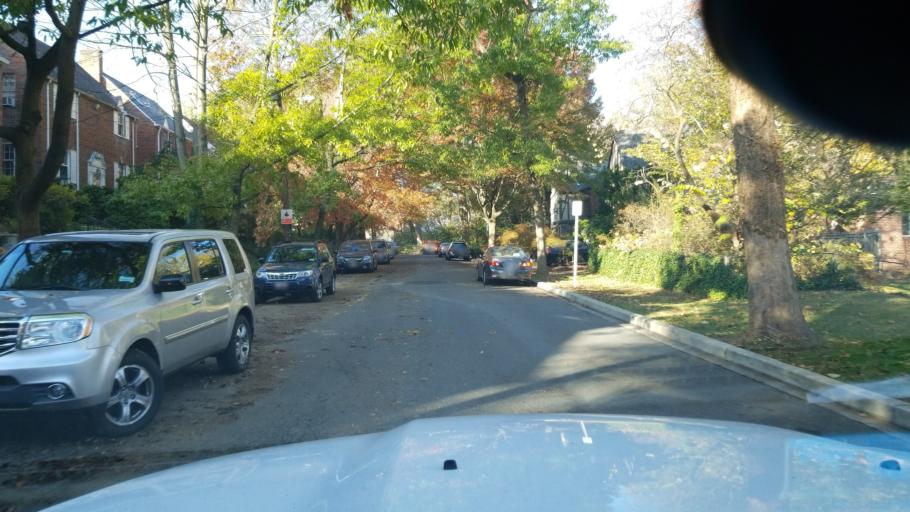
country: US
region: Maryland
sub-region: Montgomery County
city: Chevy Chase Village
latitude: 38.9555
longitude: -77.0677
